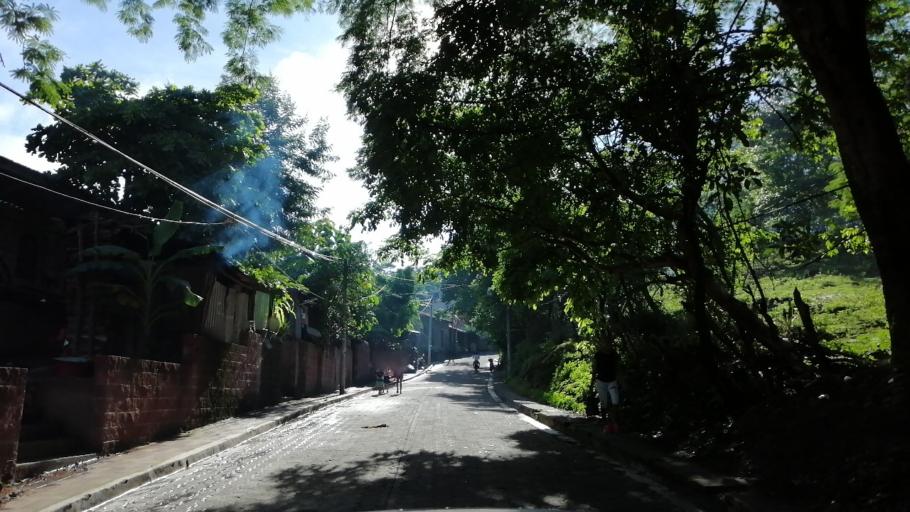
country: SV
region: Morazan
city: Cacaopera
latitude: 13.7754
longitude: -88.0840
